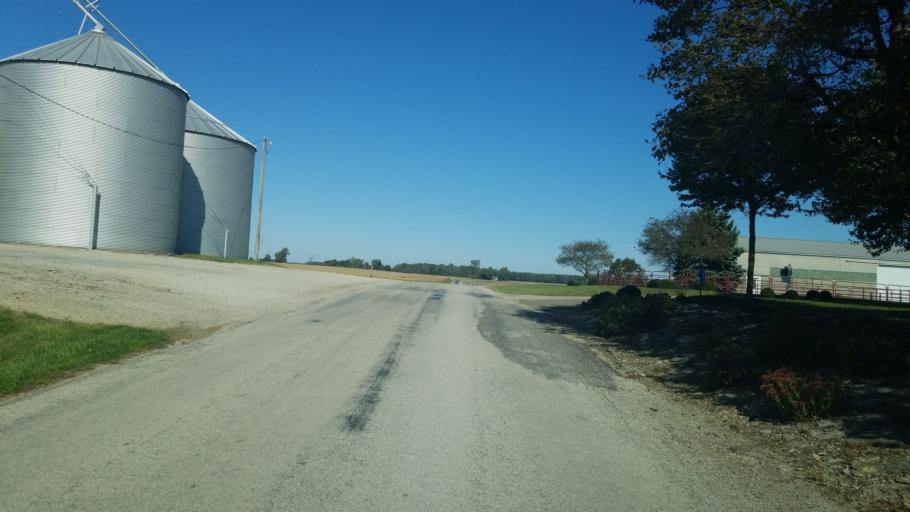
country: US
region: Ohio
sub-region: Richland County
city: Shelby
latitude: 40.8808
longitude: -82.6958
